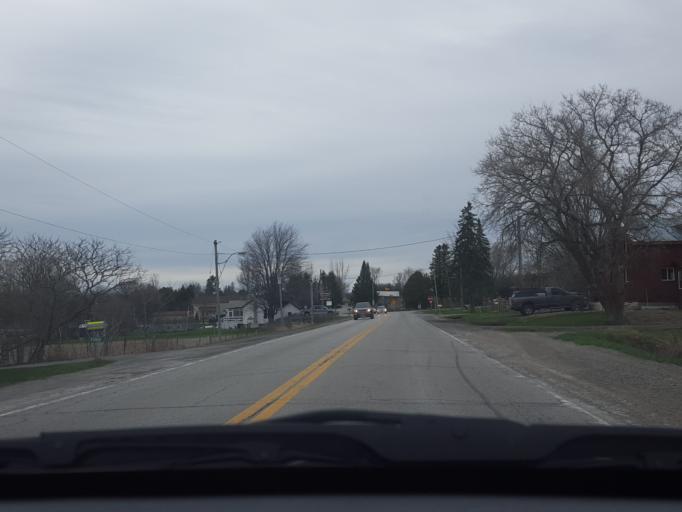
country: CA
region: Ontario
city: Uxbridge
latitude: 44.2595
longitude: -79.1348
